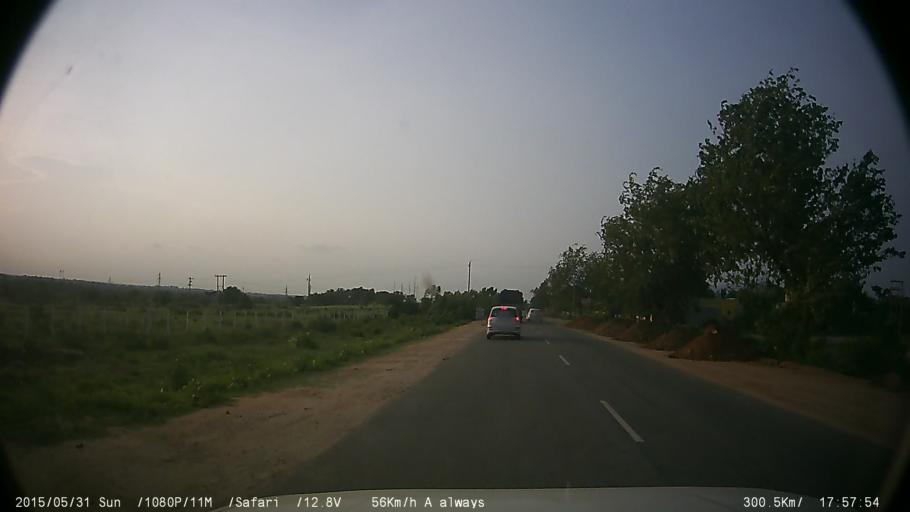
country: IN
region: Karnataka
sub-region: Mysore
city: Nanjangud
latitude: 12.0050
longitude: 76.6692
